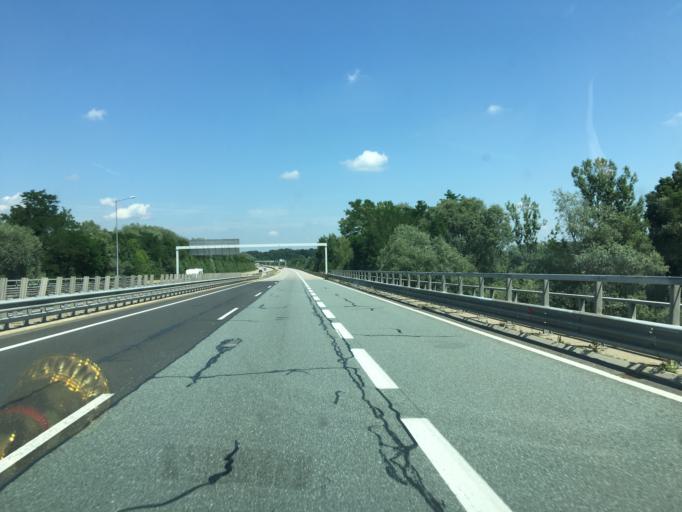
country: AT
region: Styria
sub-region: Politischer Bezirk Leibnitz
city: Spielfeld
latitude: 46.7073
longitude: 15.6409
